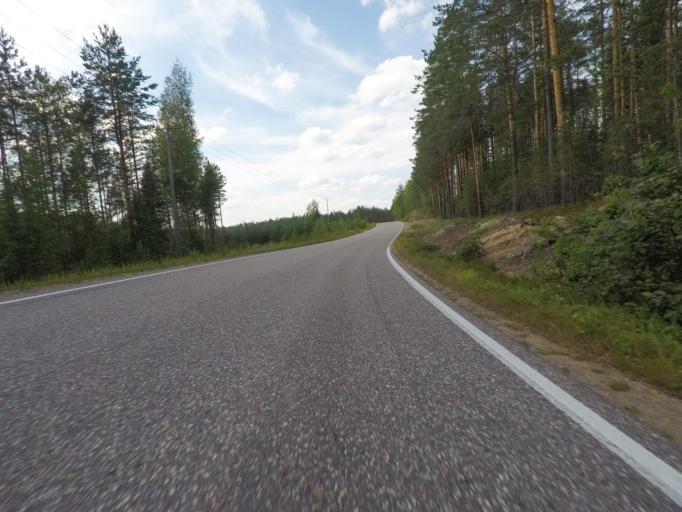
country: FI
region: Southern Savonia
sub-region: Savonlinna
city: Sulkava
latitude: 61.7371
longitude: 28.2009
